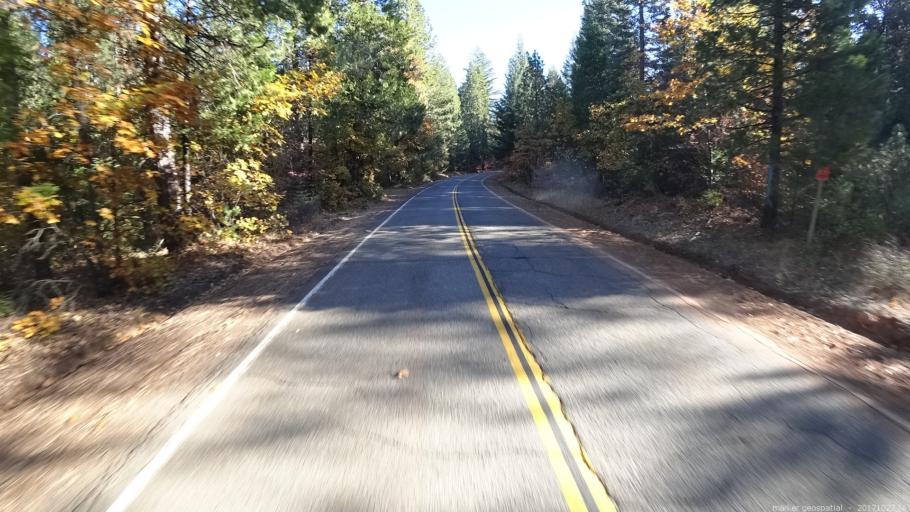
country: US
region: California
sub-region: Shasta County
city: Burney
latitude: 40.9679
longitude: -121.9346
